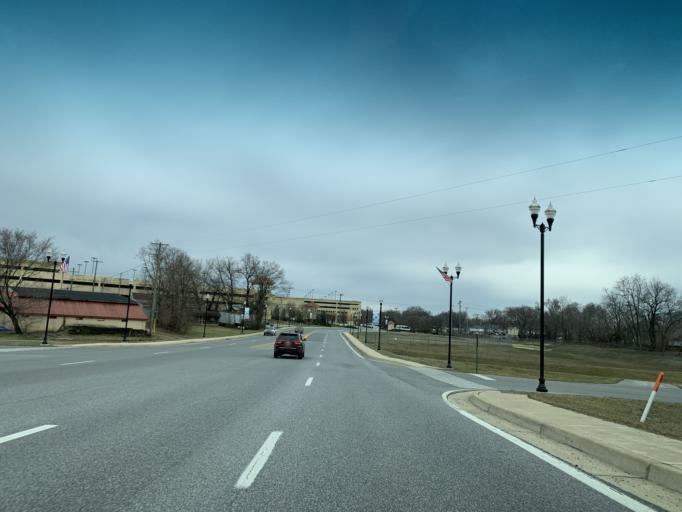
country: US
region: West Virginia
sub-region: Jefferson County
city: Ranson
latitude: 39.3001
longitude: -77.8510
